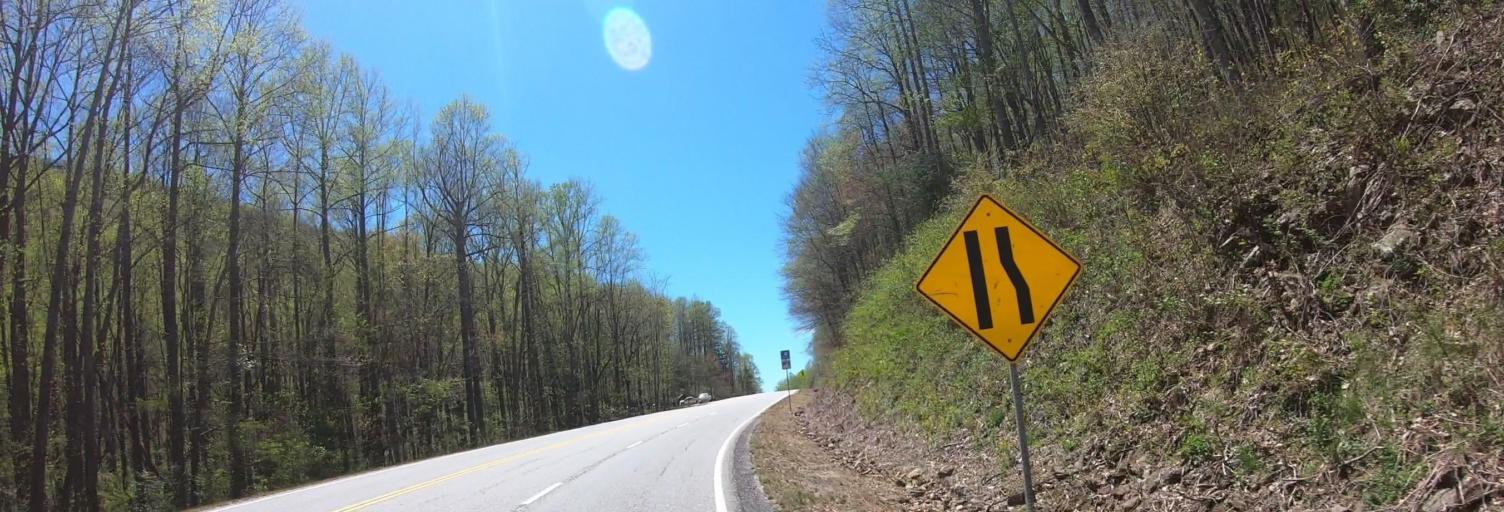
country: US
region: Georgia
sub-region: Towns County
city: Hiawassee
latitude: 34.8033
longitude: -83.7428
